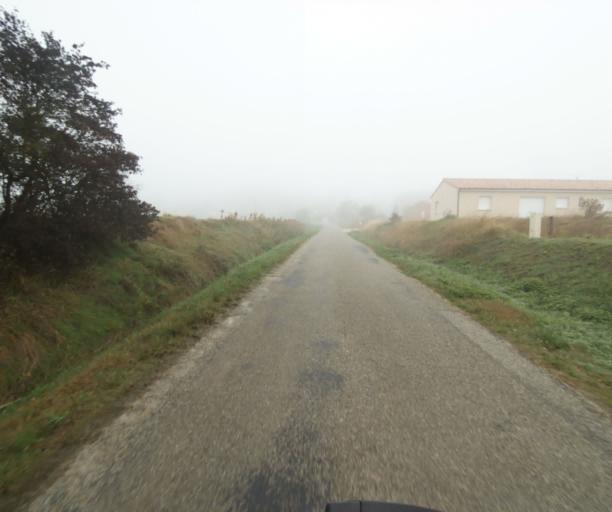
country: FR
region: Midi-Pyrenees
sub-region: Departement de la Haute-Garonne
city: Villemur-sur-Tarn
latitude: 43.9123
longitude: 1.4829
